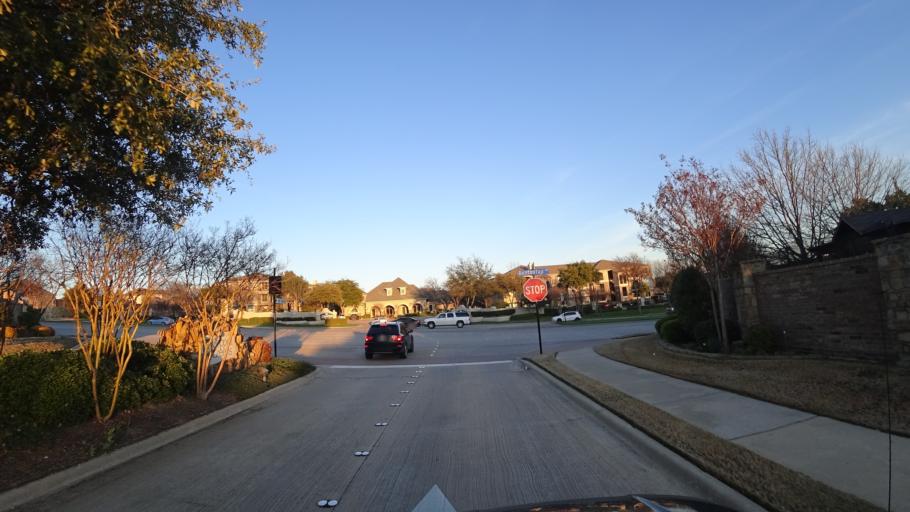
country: US
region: Texas
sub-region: Dallas County
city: Coppell
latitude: 32.9922
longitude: -96.9937
